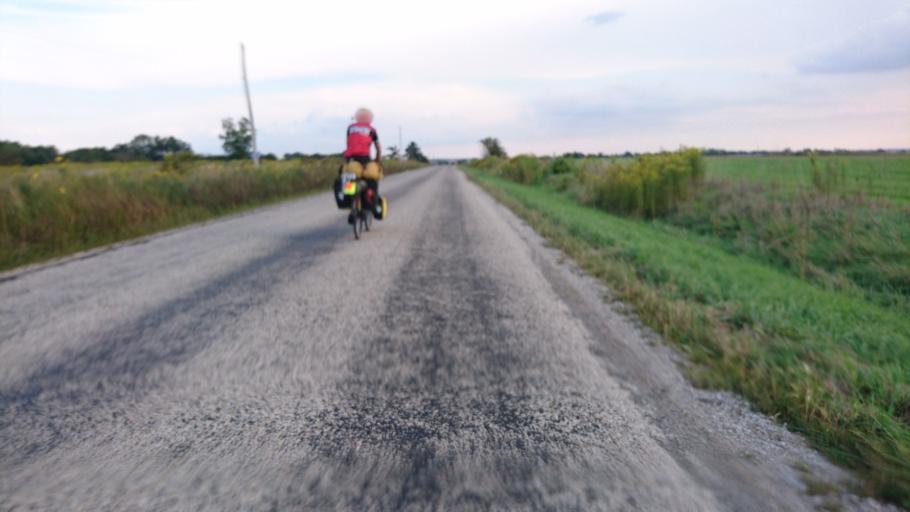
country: US
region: Illinois
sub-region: Logan County
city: Atlanta
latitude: 40.2269
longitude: -89.2017
